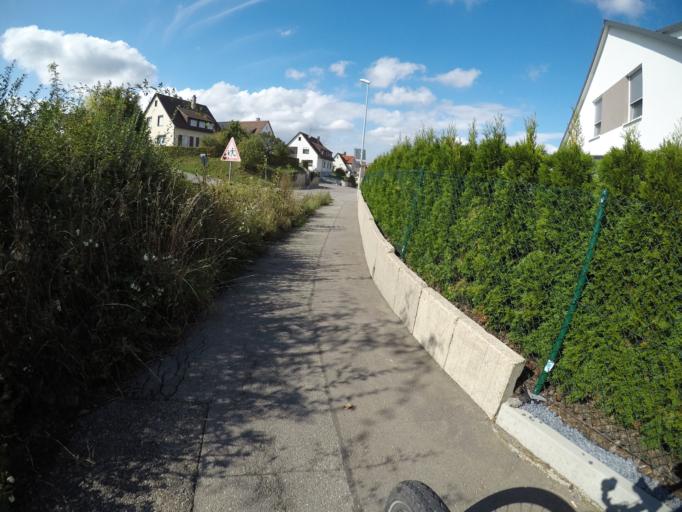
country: DE
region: Baden-Wuerttemberg
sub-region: Regierungsbezirk Stuttgart
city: Gartringen
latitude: 48.6385
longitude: 8.8939
